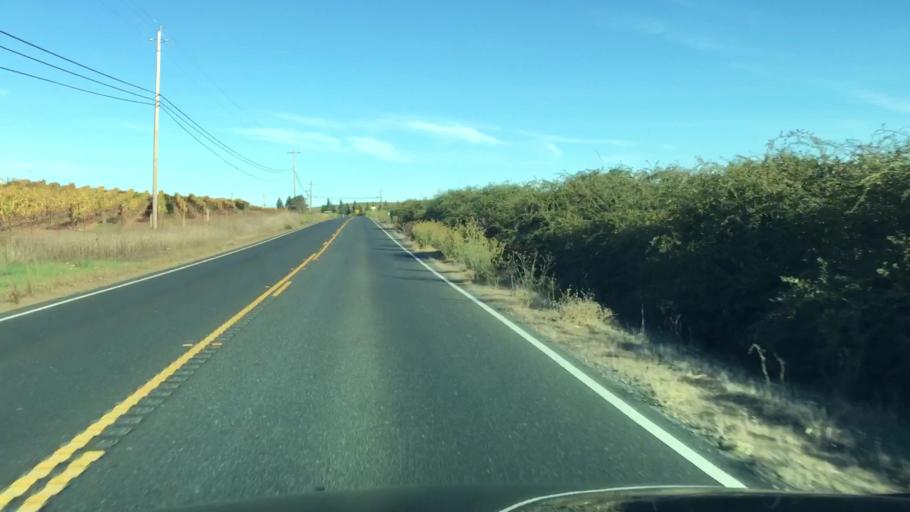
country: US
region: California
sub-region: Sonoma County
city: Temelec
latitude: 38.1970
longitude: -122.4457
